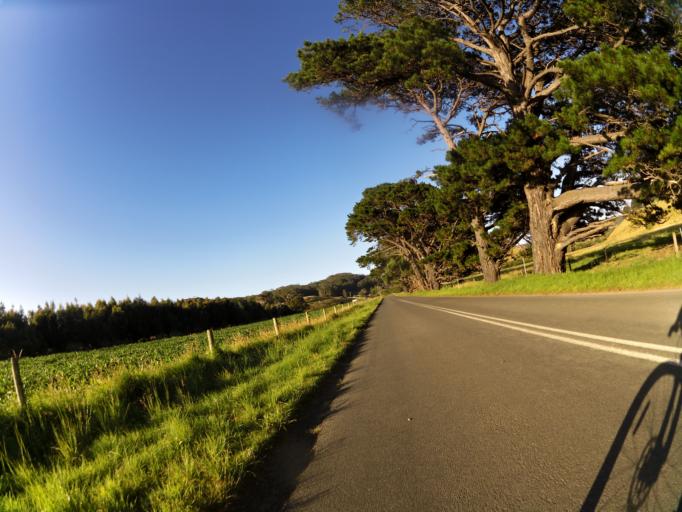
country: AU
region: Victoria
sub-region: Colac-Otway
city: Apollo Bay
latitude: -38.7681
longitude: 143.6519
